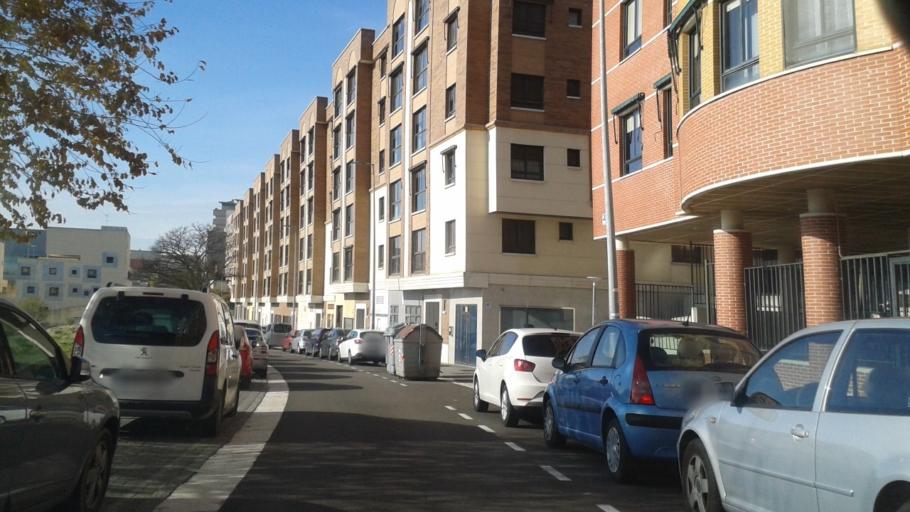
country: ES
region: Castille and Leon
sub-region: Provincia de Valladolid
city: Zaratan
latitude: 41.6354
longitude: -4.7626
